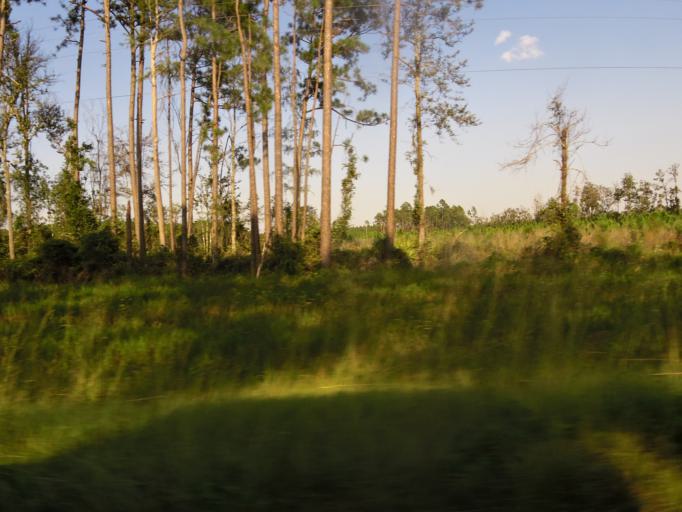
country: US
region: Florida
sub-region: Duval County
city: Baldwin
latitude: 30.3395
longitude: -82.0090
